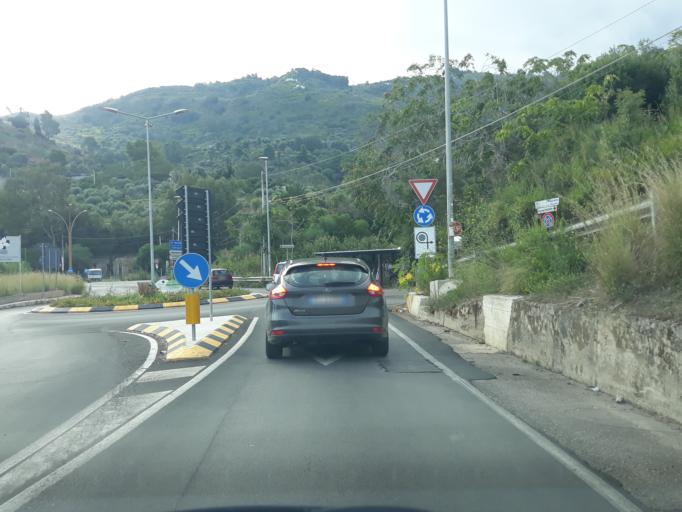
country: IT
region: Sicily
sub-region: Palermo
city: Cefalu
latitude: 38.0268
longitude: 14.0136
